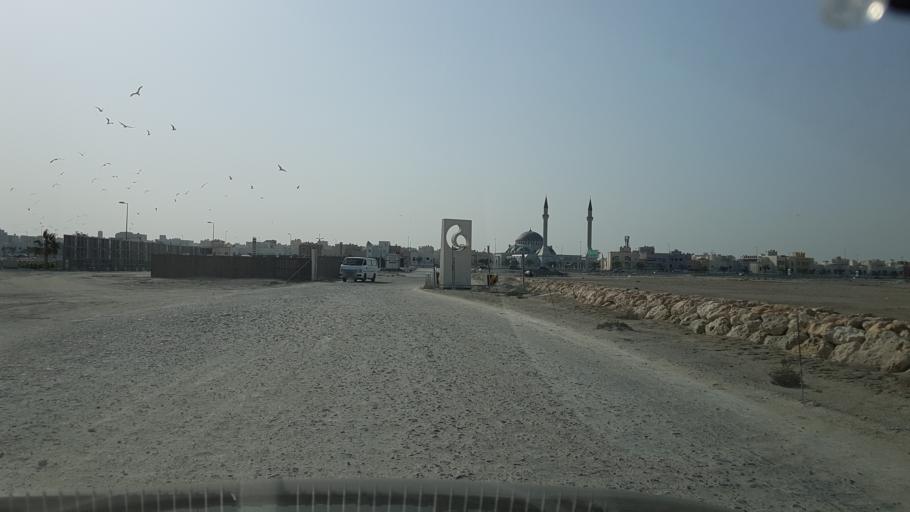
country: BH
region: Muharraq
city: Al Hadd
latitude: 26.2710
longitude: 50.6647
